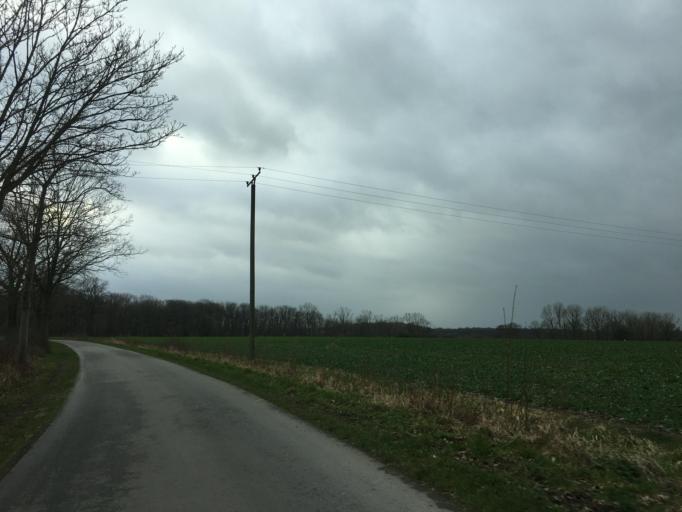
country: DE
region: North Rhine-Westphalia
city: Ludinghausen
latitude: 51.8023
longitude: 7.4619
